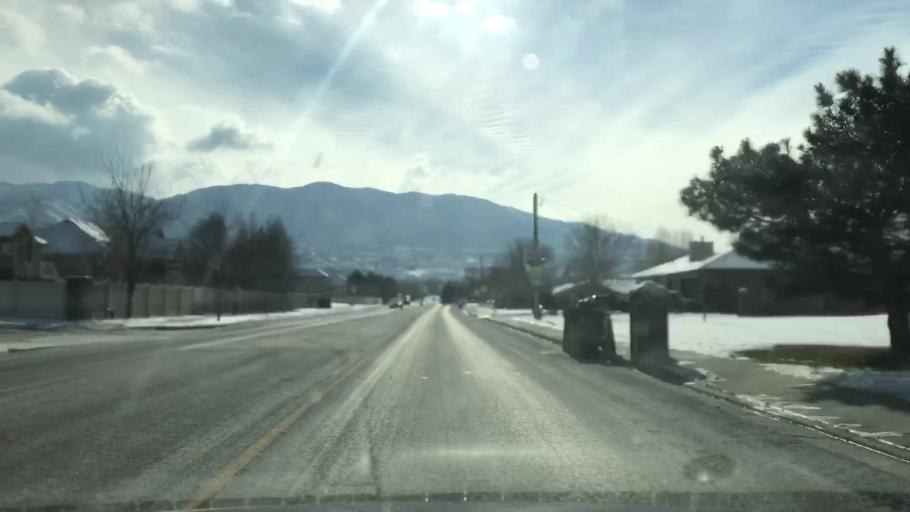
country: US
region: Utah
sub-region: Salt Lake County
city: Draper
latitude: 40.5102
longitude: -111.8818
